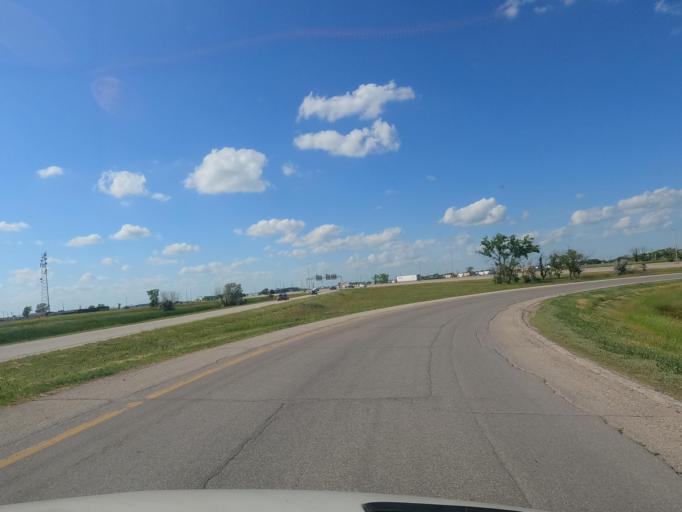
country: CA
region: Manitoba
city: Winnipeg
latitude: 49.9718
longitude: -97.0764
